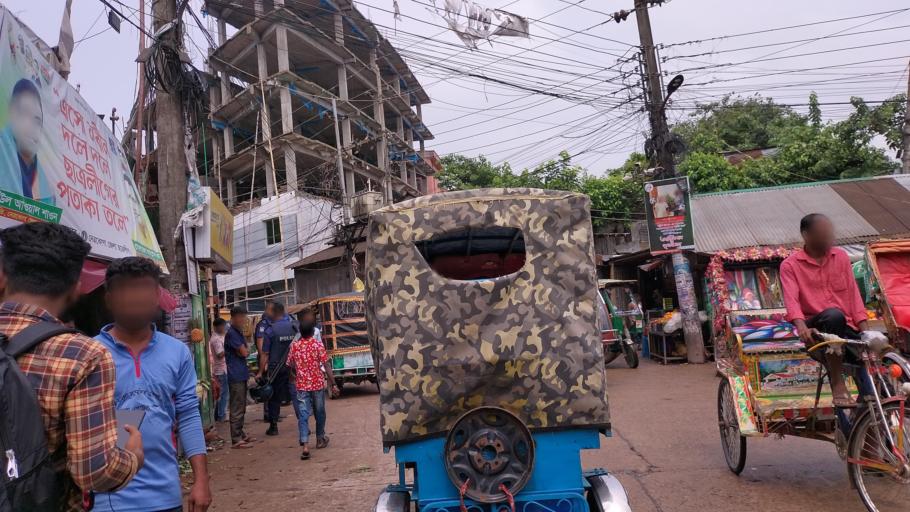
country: BD
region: Dhaka
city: Netrakona
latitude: 24.8849
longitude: 90.7338
